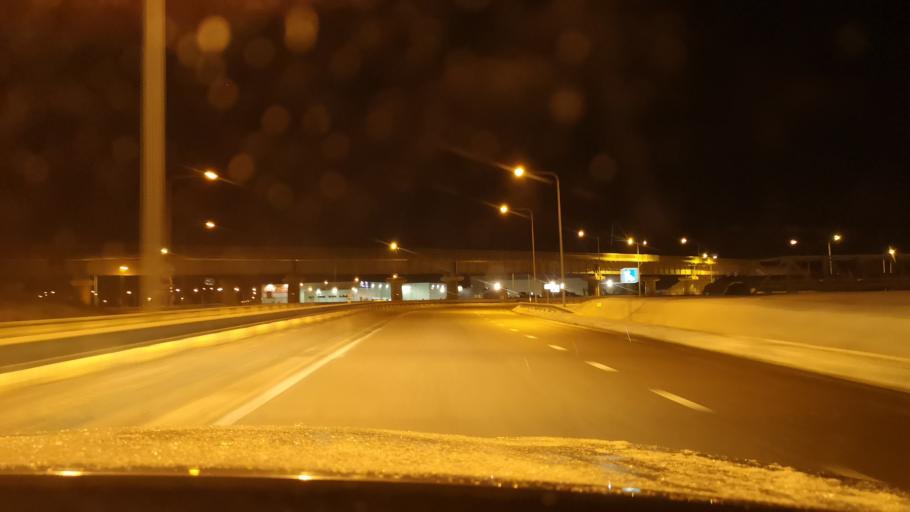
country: EE
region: Harju
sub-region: Joelaehtme vald
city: Loo
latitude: 59.4478
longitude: 24.9247
